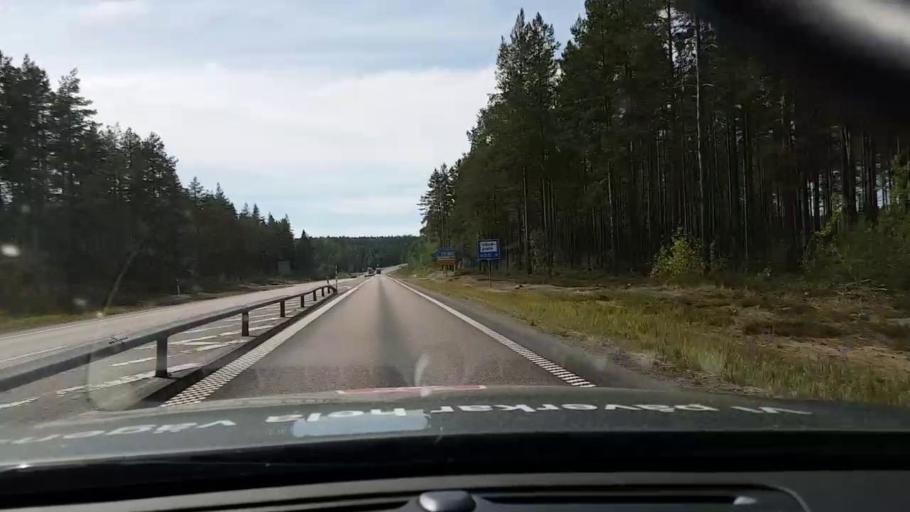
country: SE
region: Vaesternorrland
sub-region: OErnskoeldsviks Kommun
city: Husum
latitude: 63.3168
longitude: 19.0112
